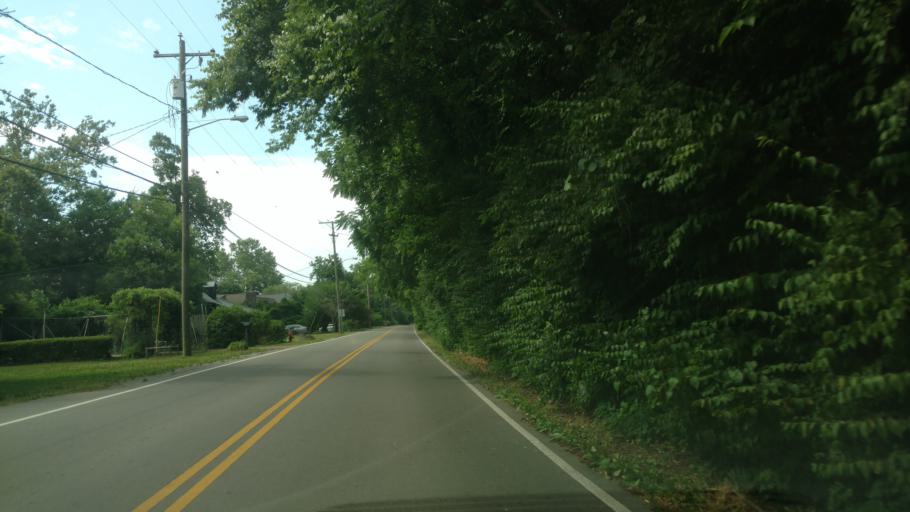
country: US
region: Tennessee
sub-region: Davidson County
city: Lakewood
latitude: 36.2200
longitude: -86.7056
